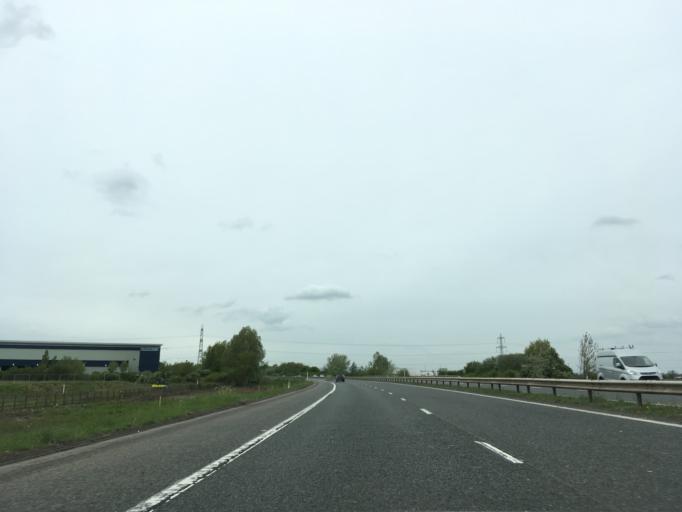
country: GB
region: England
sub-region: South Gloucestershire
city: Severn Beach
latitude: 51.5459
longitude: -2.6380
